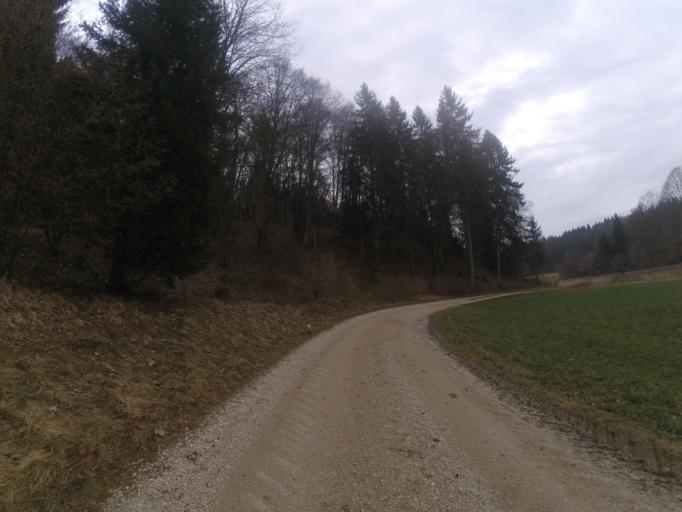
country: DE
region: Baden-Wuerttemberg
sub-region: Tuebingen Region
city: Mehrstetten
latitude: 48.3594
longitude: 9.5443
